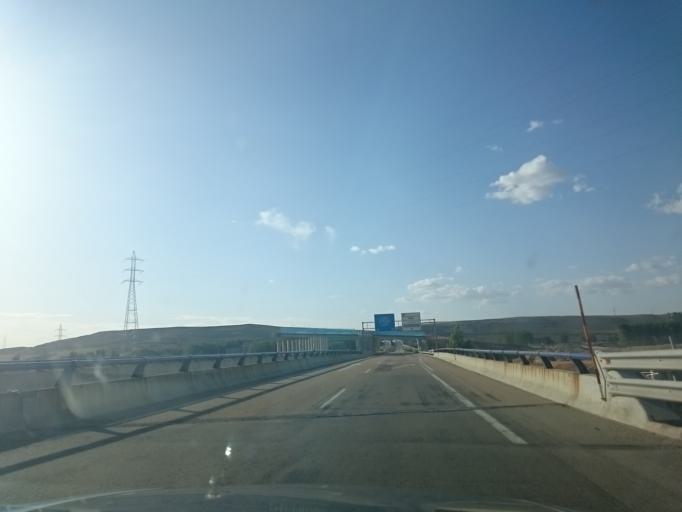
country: ES
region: Castille and Leon
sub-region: Provincia de Burgos
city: San Mames de Burgos
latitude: 42.3432
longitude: -3.7903
